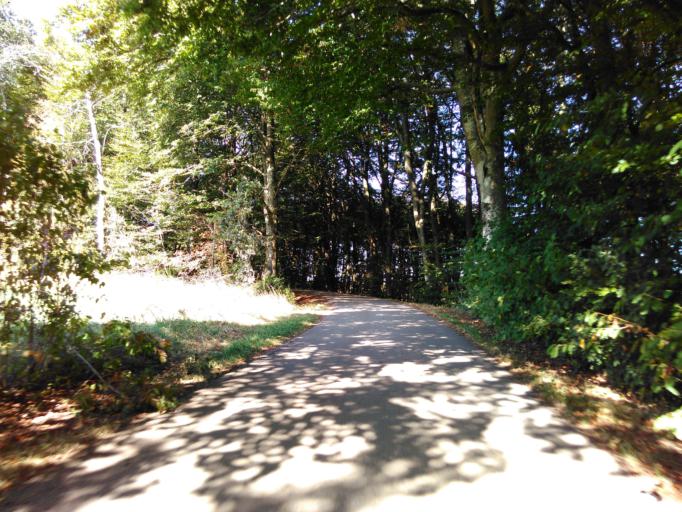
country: LU
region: Diekirch
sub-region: Canton de Redange
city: Rambrouch
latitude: 49.8136
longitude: 5.8390
